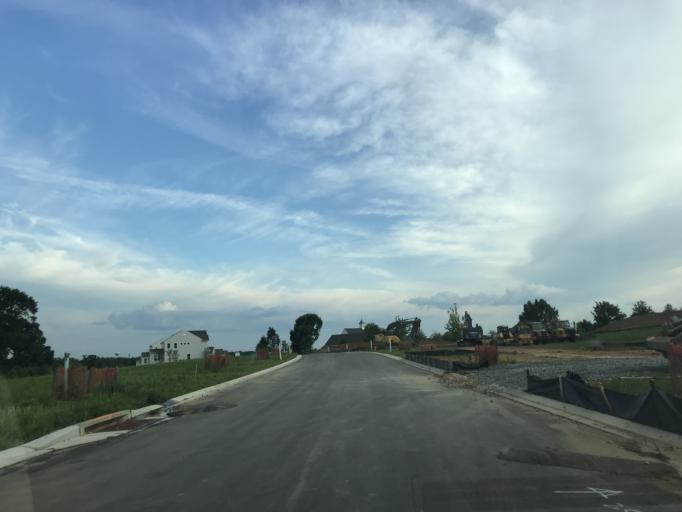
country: US
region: Maryland
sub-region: Harford County
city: Perryman
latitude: 39.5025
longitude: -76.2069
